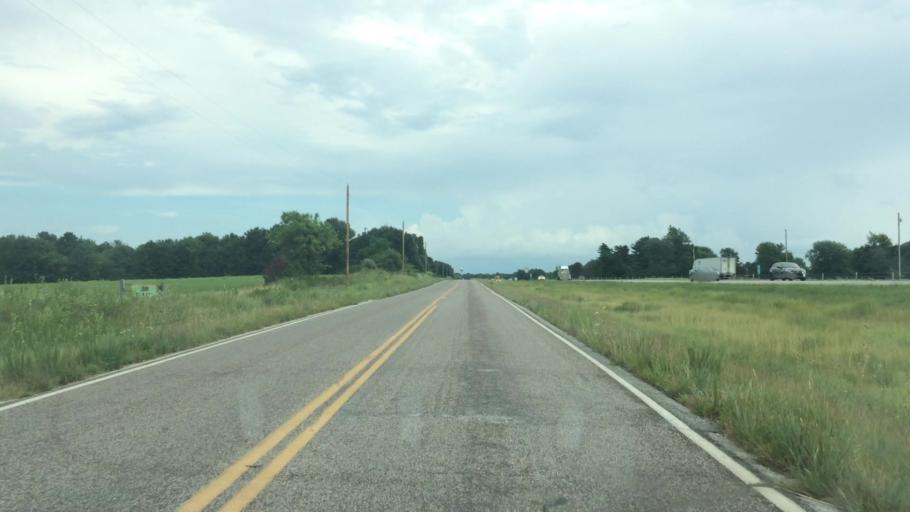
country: US
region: Missouri
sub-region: Greene County
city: Strafford
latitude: 37.2615
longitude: -93.1515
